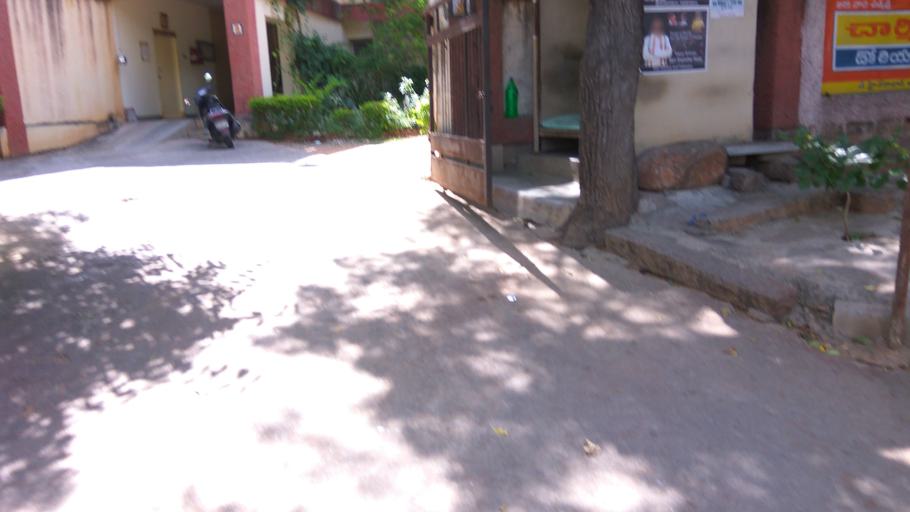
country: IN
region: Telangana
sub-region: Rangareddi
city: Kukatpalli
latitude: 17.4554
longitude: 78.4396
